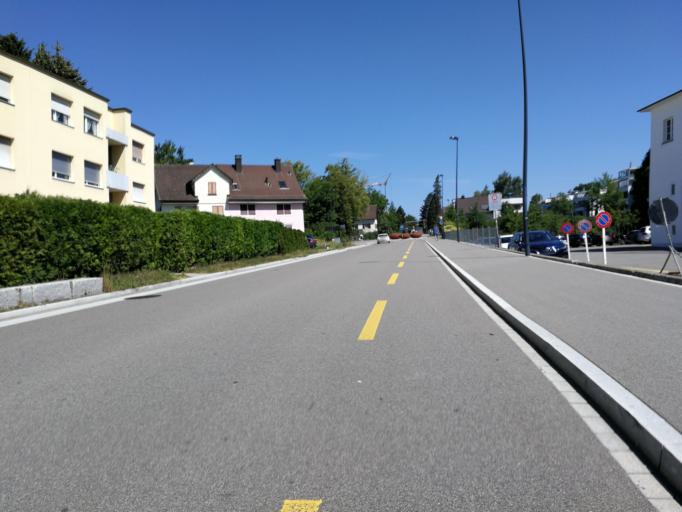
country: CH
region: Zurich
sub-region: Bezirk Uster
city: Uster / Nieder-Uster
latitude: 47.3462
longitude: 8.7017
